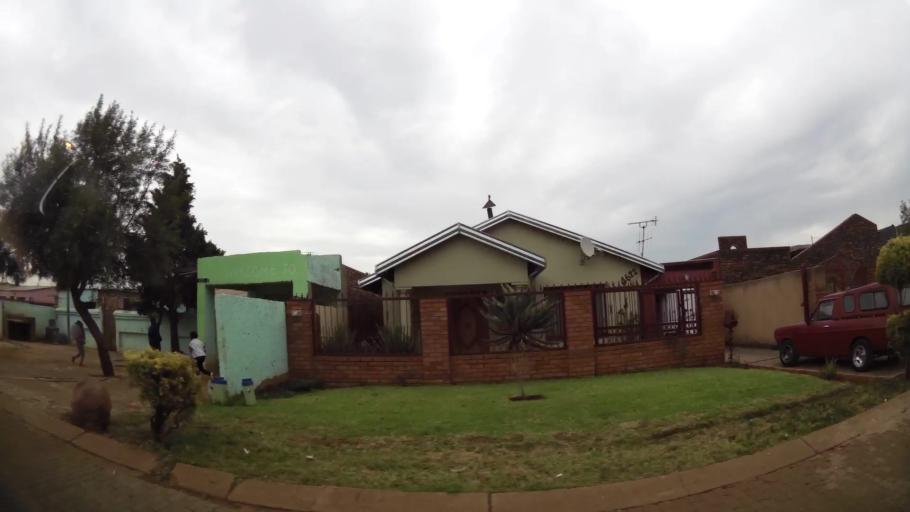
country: ZA
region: Gauteng
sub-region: City of Tshwane Metropolitan Municipality
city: Cullinan
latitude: -25.7062
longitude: 28.3634
